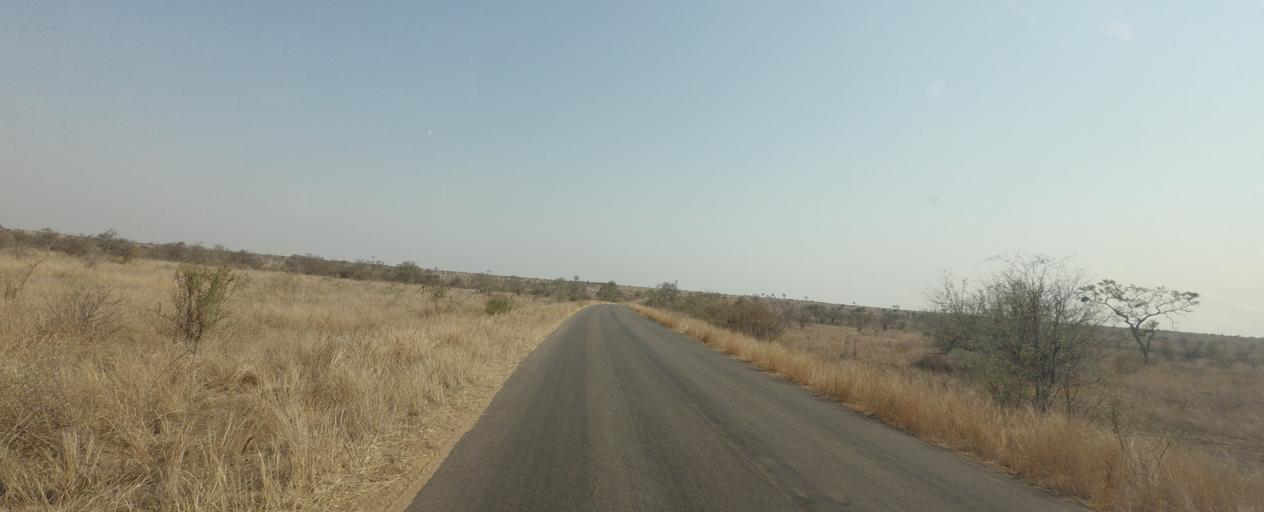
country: ZA
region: Limpopo
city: Thulamahashi
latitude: -24.3658
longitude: 31.7643
